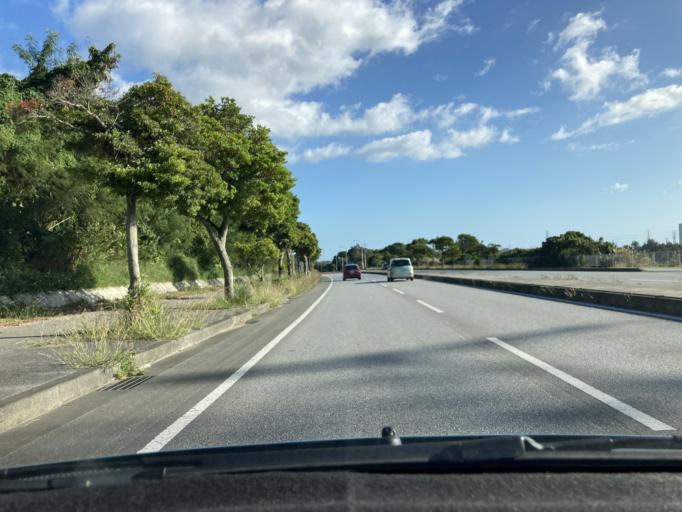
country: JP
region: Okinawa
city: Ishikawa
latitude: 26.4049
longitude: 127.8228
